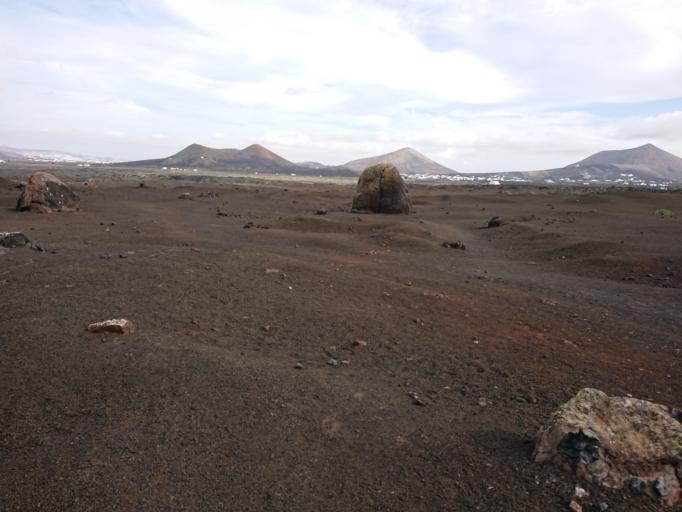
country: ES
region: Canary Islands
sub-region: Provincia de Las Palmas
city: Tias
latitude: 29.0038
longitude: -13.6766
